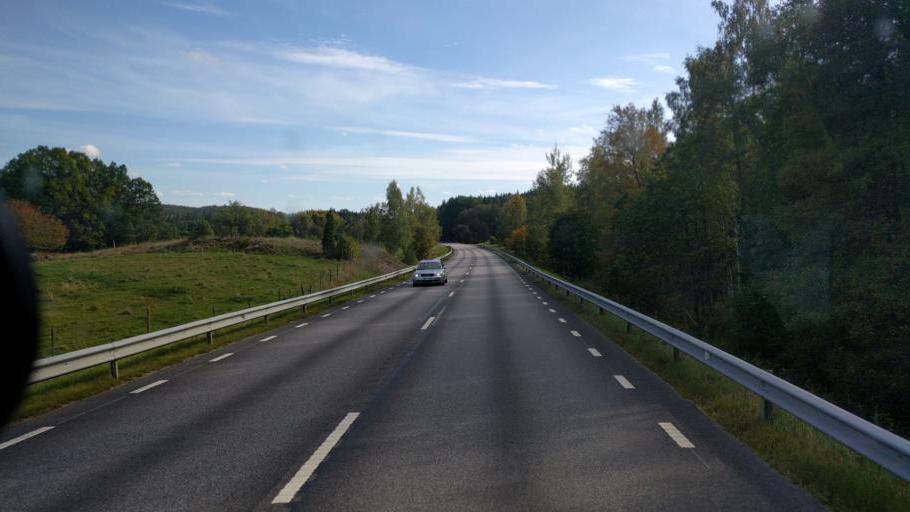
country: SE
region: OEstergoetland
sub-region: Kinda Kommun
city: Kisa
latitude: 57.9155
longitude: 15.6855
